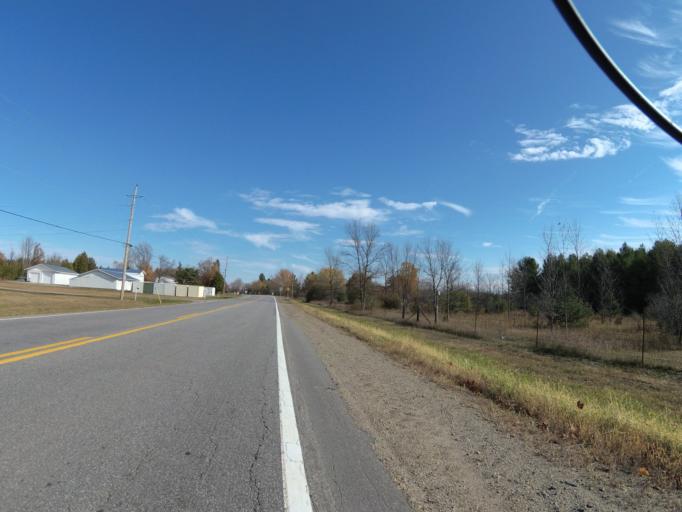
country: CA
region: Ontario
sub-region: Lanark County
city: Smiths Falls
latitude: 44.8388
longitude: -75.9422
